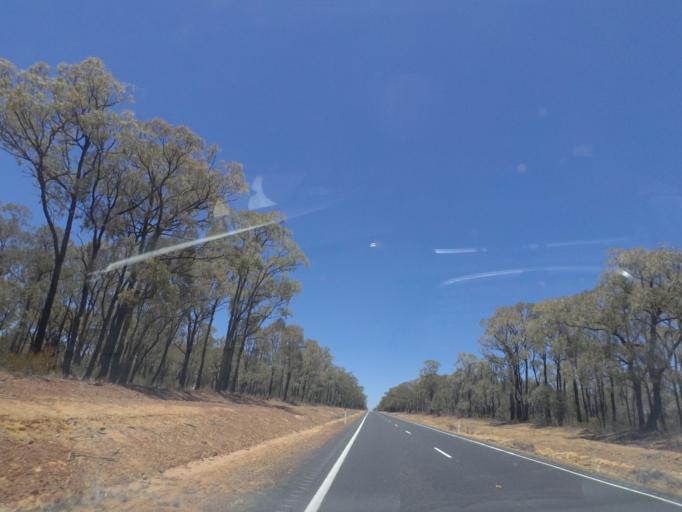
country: AU
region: New South Wales
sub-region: Narrabri
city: Narrabri
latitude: -30.7314
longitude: 149.5203
